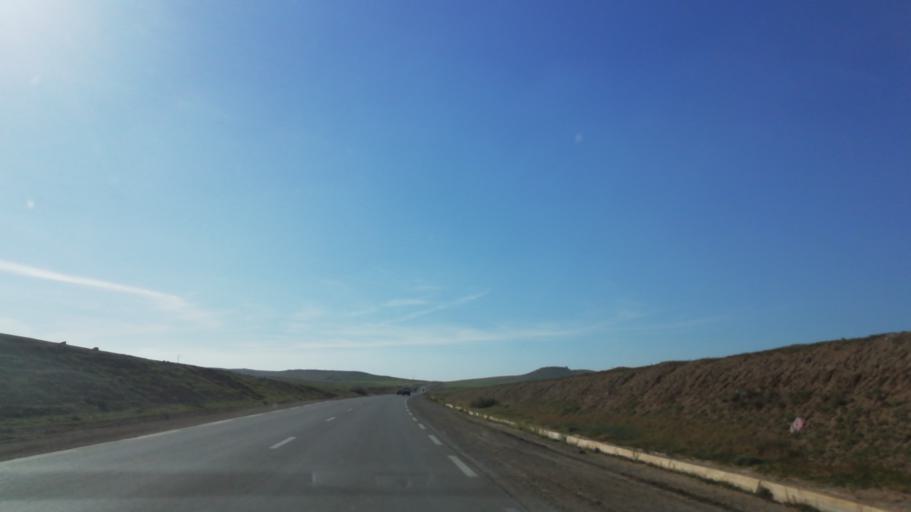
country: DZ
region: Mascara
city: Oued el Abtal
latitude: 35.4461
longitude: 0.5958
